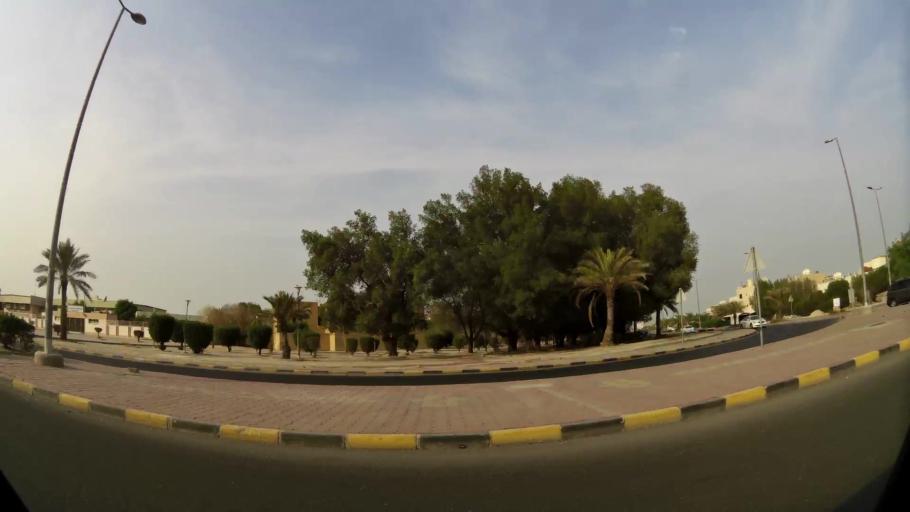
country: KW
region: Mubarak al Kabir
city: Sabah as Salim
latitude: 29.2568
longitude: 48.0542
